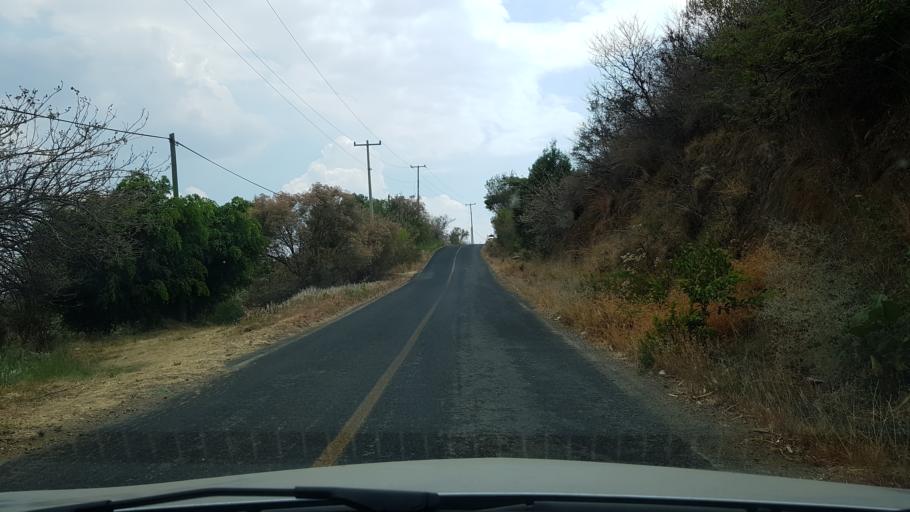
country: MX
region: Puebla
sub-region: Tochimilco
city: San Antonio Alpanocan
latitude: 18.8445
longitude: -98.7154
